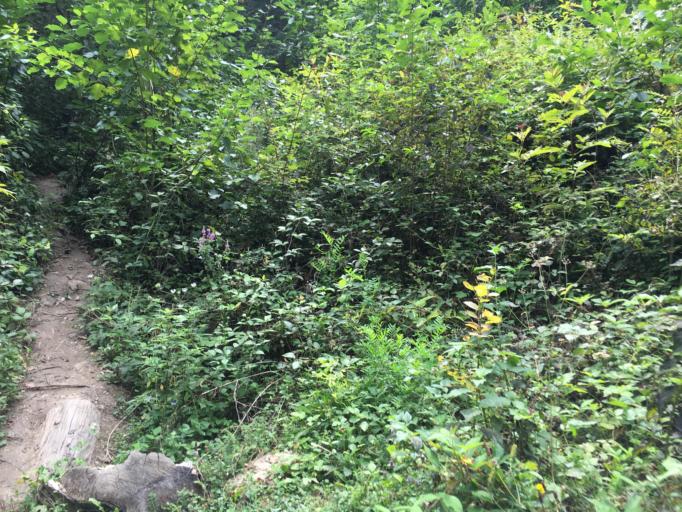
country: RU
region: Krasnodarskiy
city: Tuapse
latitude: 44.2588
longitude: 39.2176
